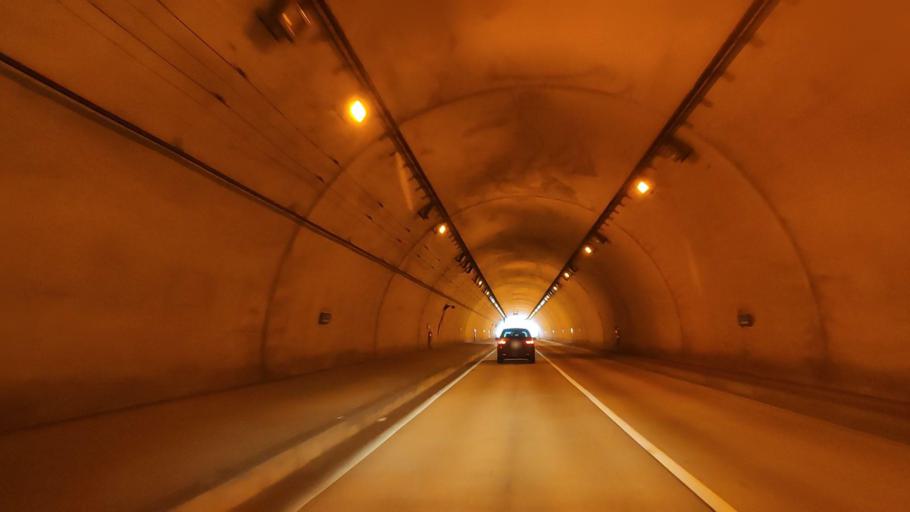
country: JP
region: Ehime
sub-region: Shikoku-chuo Shi
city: Matsuyama
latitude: 33.8857
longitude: 132.7080
